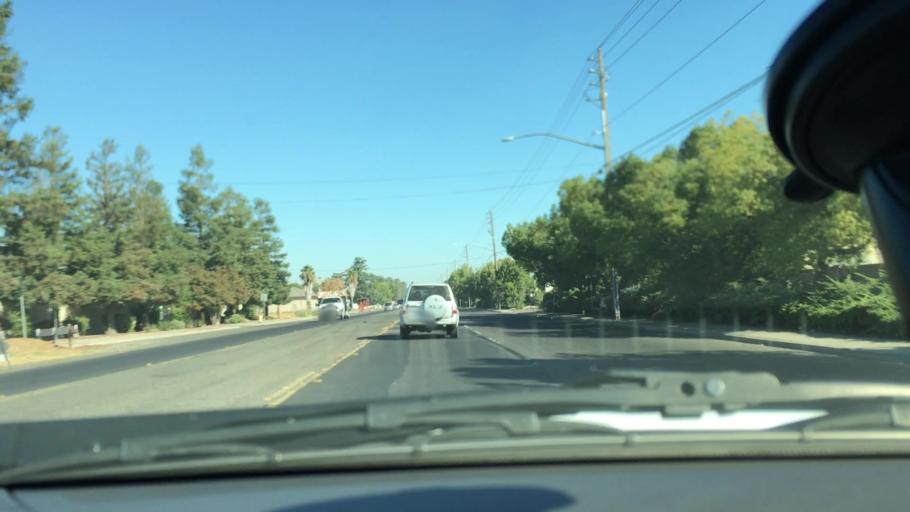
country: US
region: California
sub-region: Stanislaus County
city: West Modesto
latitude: 37.6249
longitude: -121.0304
